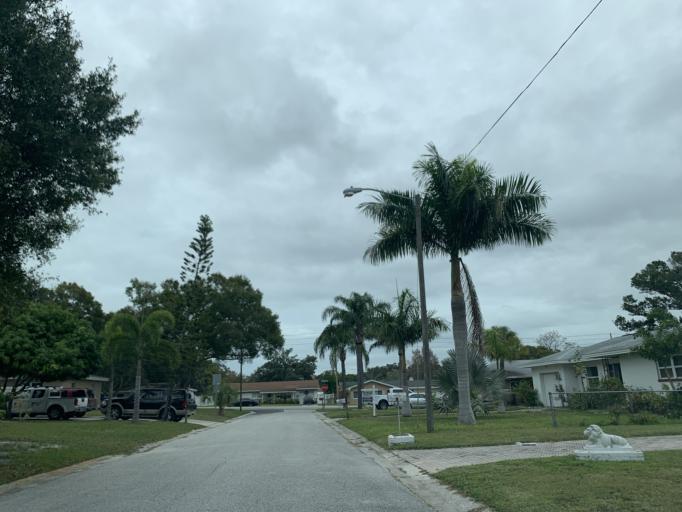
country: US
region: Florida
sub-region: Pinellas County
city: Belleair
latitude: 27.9382
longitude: -82.7823
